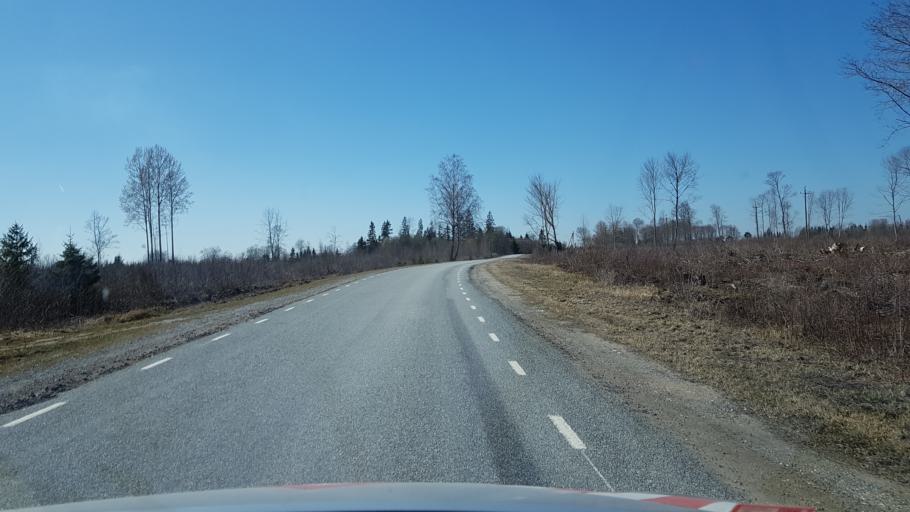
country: EE
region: Laeaene-Virumaa
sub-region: Vaeike-Maarja vald
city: Vaike-Maarja
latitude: 59.1250
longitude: 26.2863
